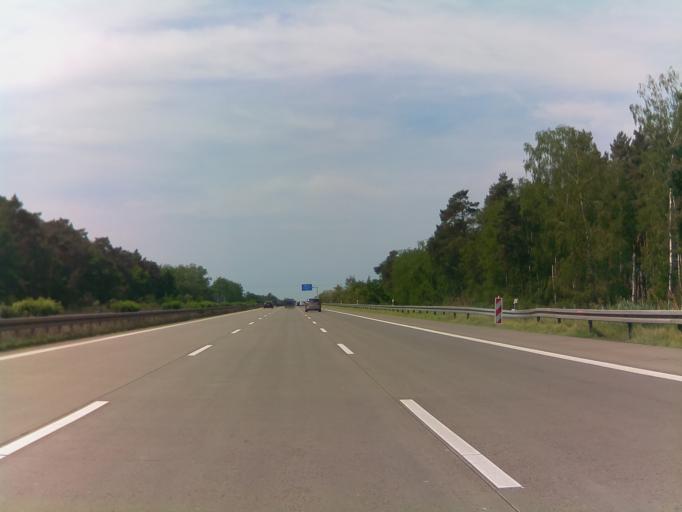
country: DE
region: Saxony-Anhalt
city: Schermen
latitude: 52.2270
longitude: 11.8442
